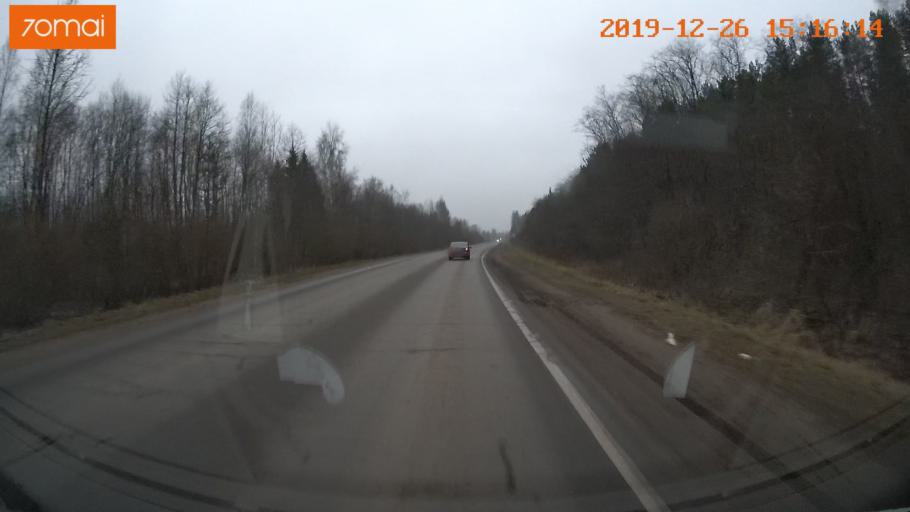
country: RU
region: Jaroslavl
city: Rybinsk
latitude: 58.0885
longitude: 38.8686
